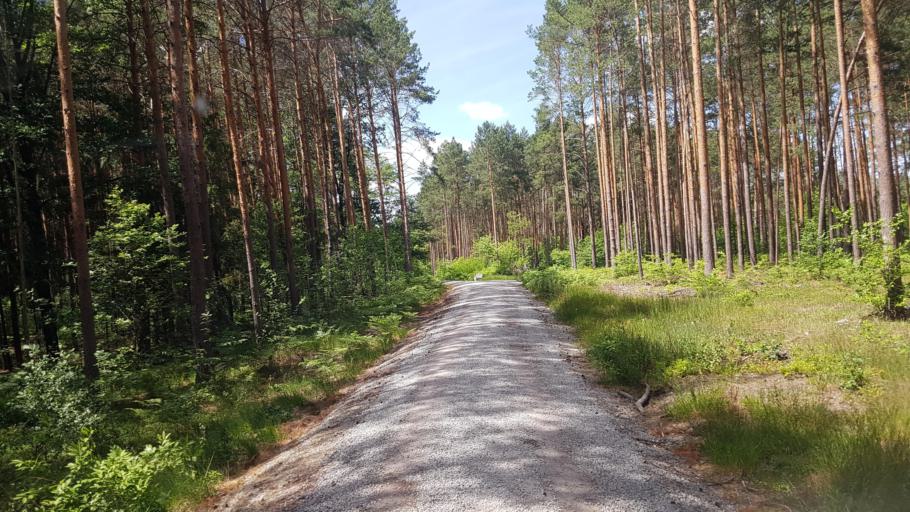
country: DE
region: Brandenburg
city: Plessa
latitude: 51.4953
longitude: 13.5953
